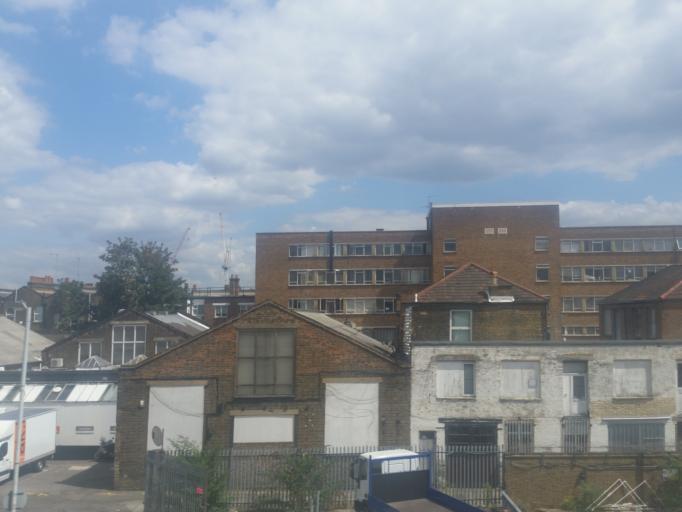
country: GB
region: England
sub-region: Greater London
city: Kennington
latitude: 51.4885
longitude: -0.0974
